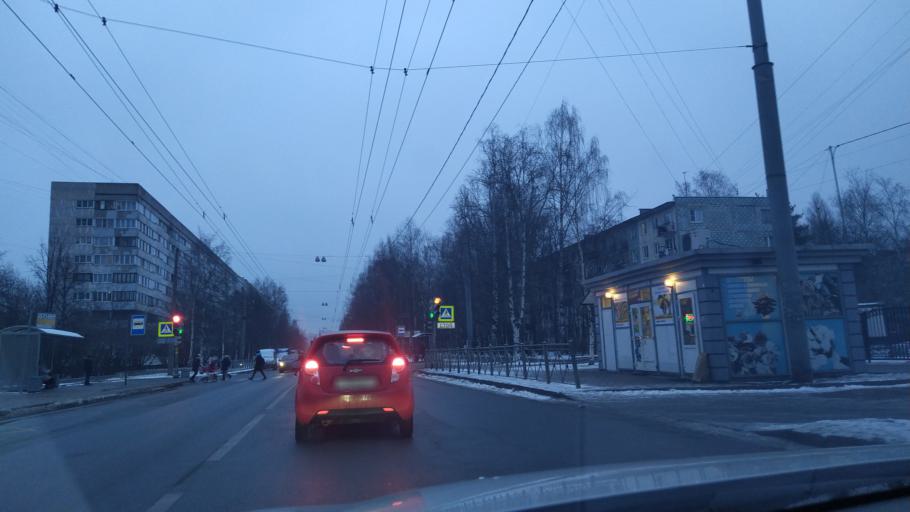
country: RU
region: Leningrad
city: Akademicheskoe
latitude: 60.0143
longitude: 30.4124
